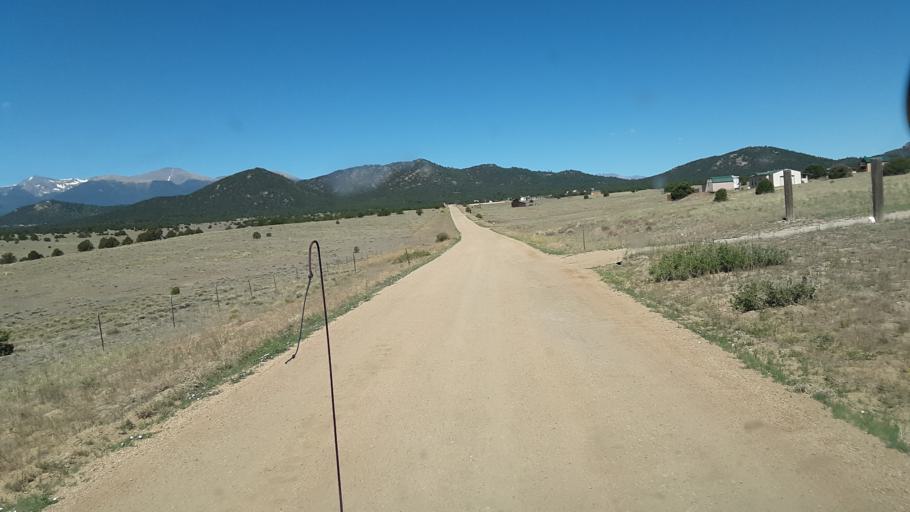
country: US
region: Colorado
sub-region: Custer County
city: Westcliffe
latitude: 38.2849
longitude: -105.5106
